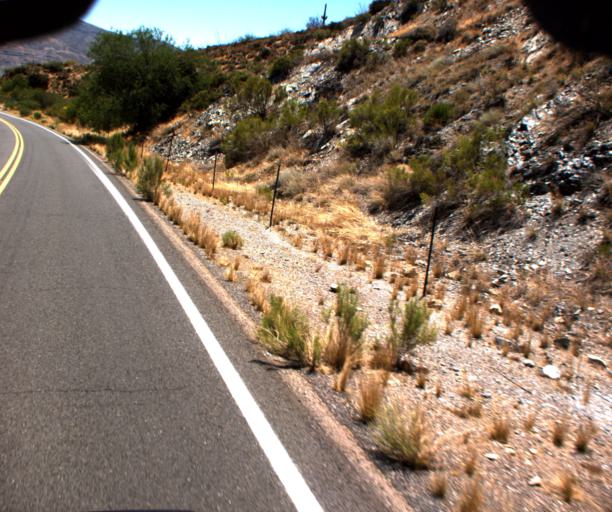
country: US
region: Arizona
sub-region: Pinal County
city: Superior
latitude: 33.1749
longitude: -111.0319
